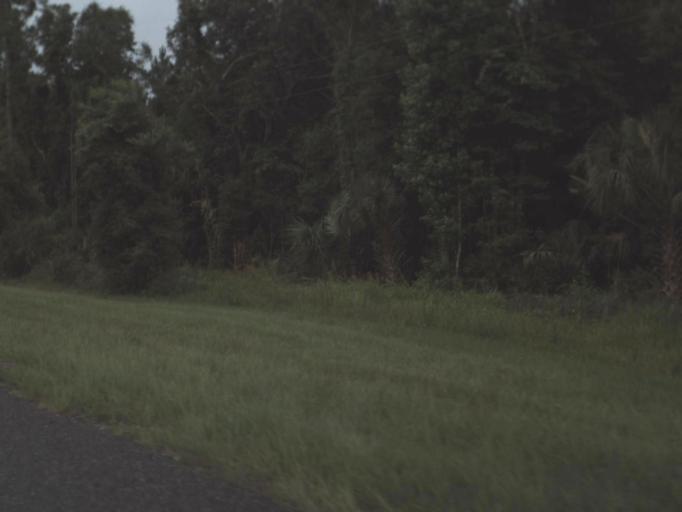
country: US
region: Florida
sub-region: Levy County
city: Inglis
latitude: 29.1739
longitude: -82.6577
